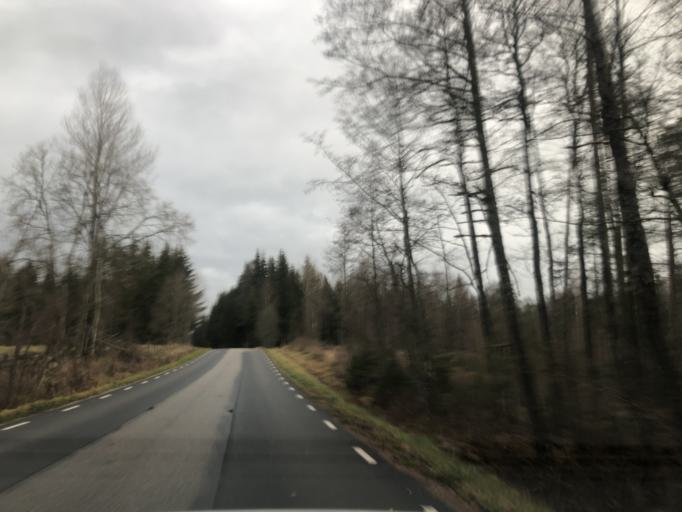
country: SE
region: Vaestra Goetaland
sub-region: Boras Kommun
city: Dalsjofors
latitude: 57.8174
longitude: 13.1968
